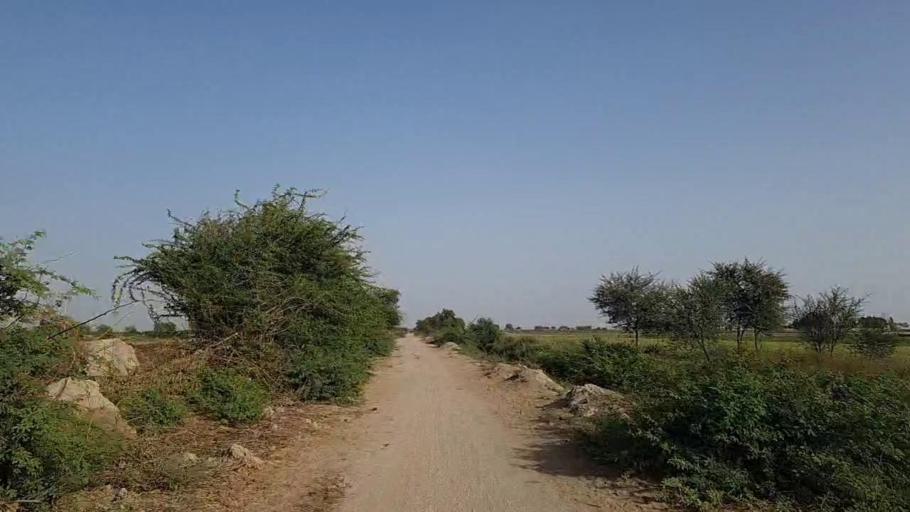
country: PK
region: Sindh
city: Jati
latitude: 24.2634
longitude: 68.1695
